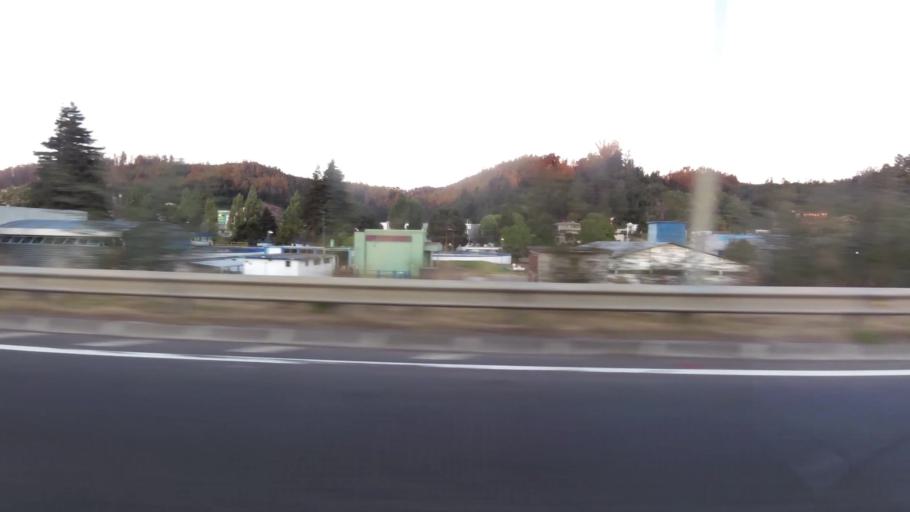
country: CL
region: Biobio
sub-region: Provincia de Concepcion
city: Concepcion
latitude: -36.8480
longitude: -73.0547
